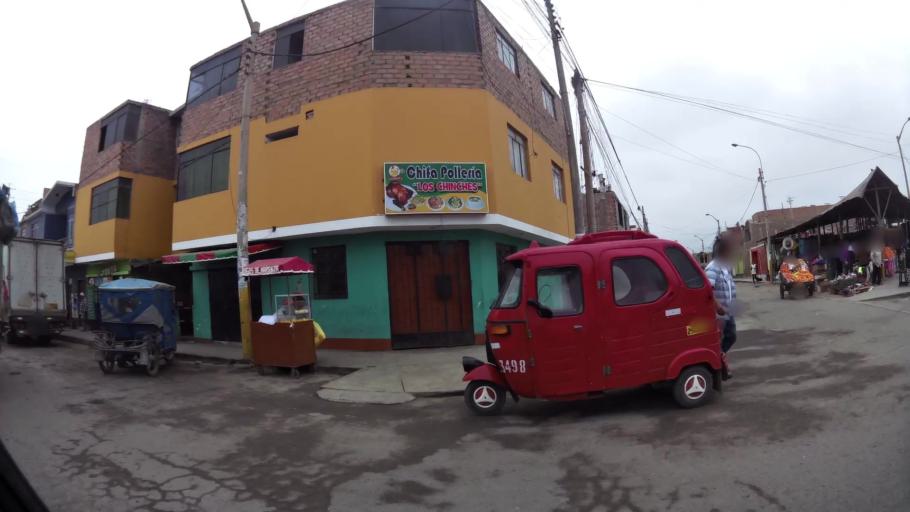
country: PE
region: Lima
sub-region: Barranca
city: Barranca
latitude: -10.7487
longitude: -77.7530
